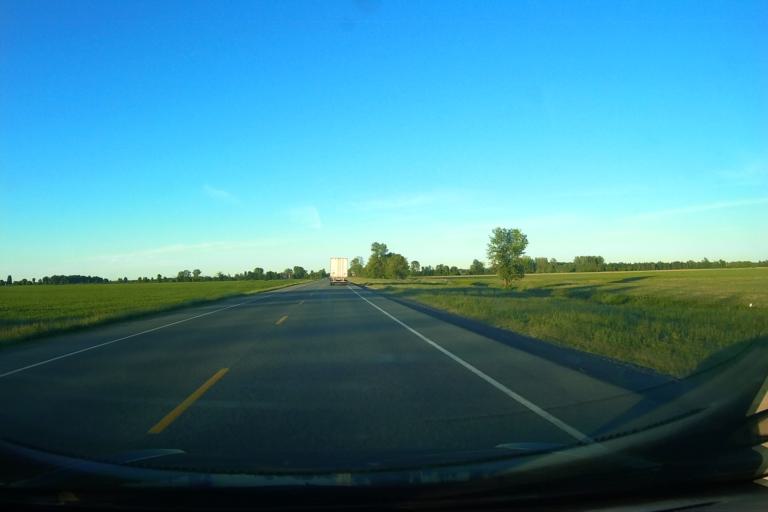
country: CA
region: Ontario
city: Prescott
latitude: 45.0526
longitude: -75.4703
